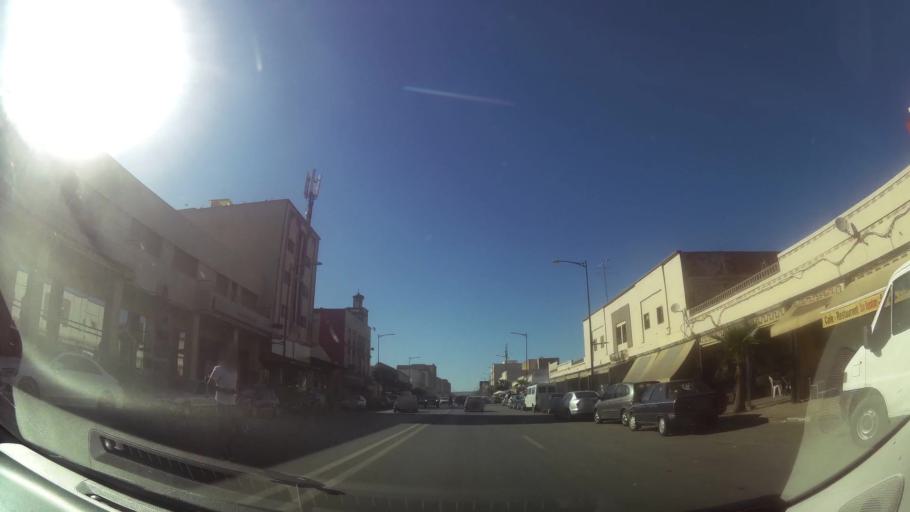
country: MA
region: Oriental
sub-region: Berkane-Taourirt
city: Ahfir
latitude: 34.8592
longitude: -1.9938
